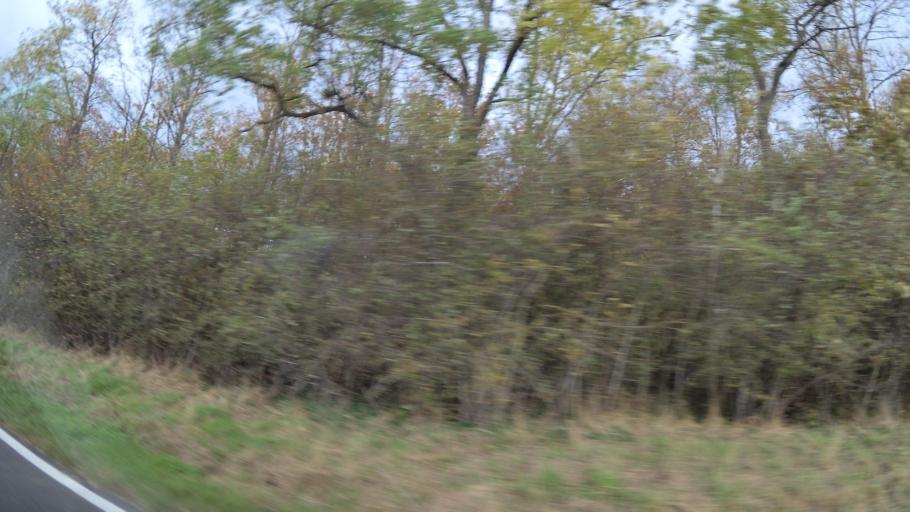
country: DE
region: Rheinland-Pfalz
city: Dietrichingen
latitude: 49.1898
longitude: 7.4232
